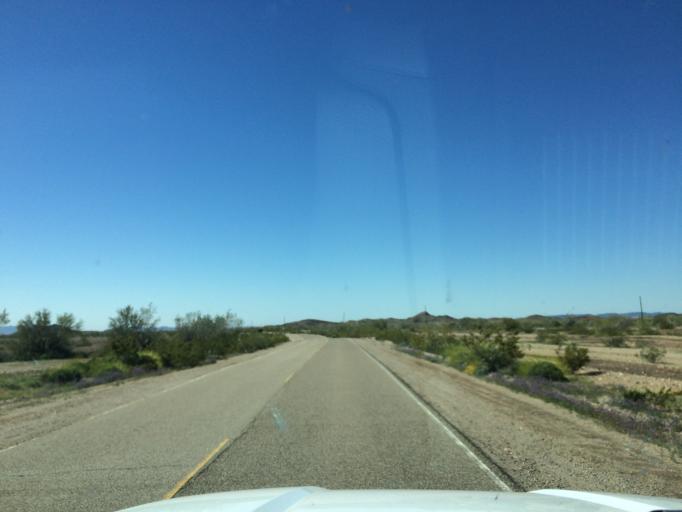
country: US
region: Arizona
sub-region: Yuma County
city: Wellton
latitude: 32.9652
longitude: -114.2896
